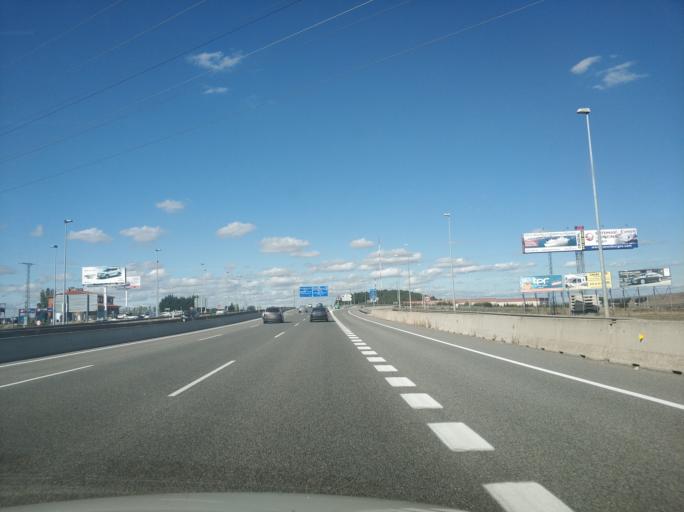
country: ES
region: Castille and Leon
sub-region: Provincia de Burgos
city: Villagonzalo-Pedernales
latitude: 42.3054
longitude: -3.7024
